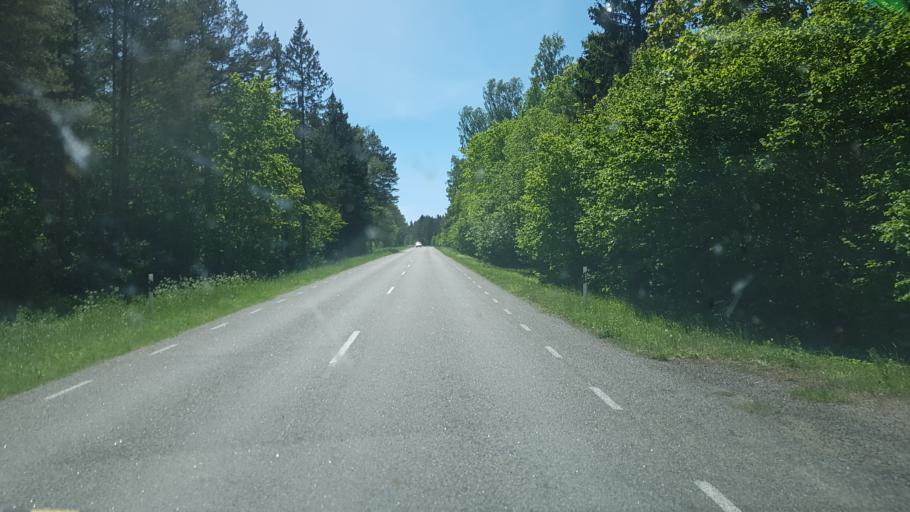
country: EE
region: Saare
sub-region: Kuressaare linn
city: Kuressaare
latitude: 58.0166
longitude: 22.1694
